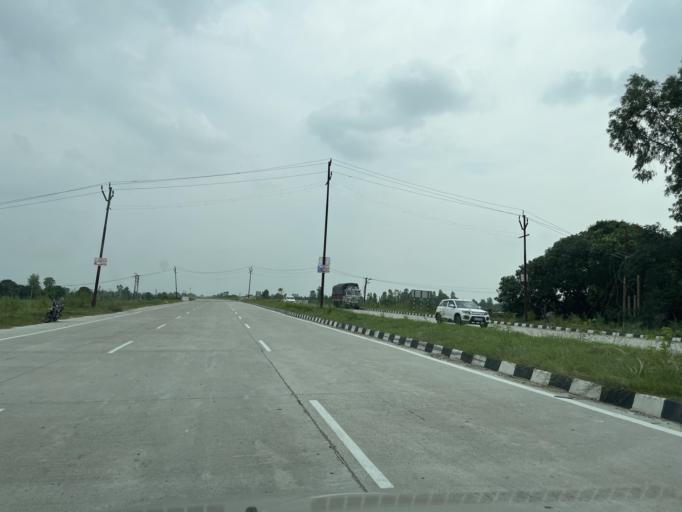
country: IN
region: Uttarakhand
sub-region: Udham Singh Nagar
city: Kashipur
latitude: 29.2031
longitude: 78.9320
